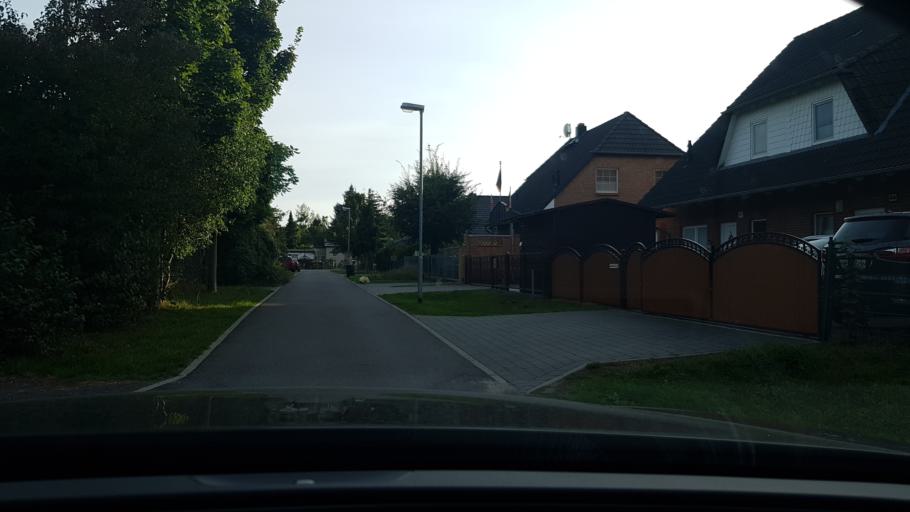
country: DE
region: Brandenburg
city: Brieselang
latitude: 52.5917
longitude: 12.9861
